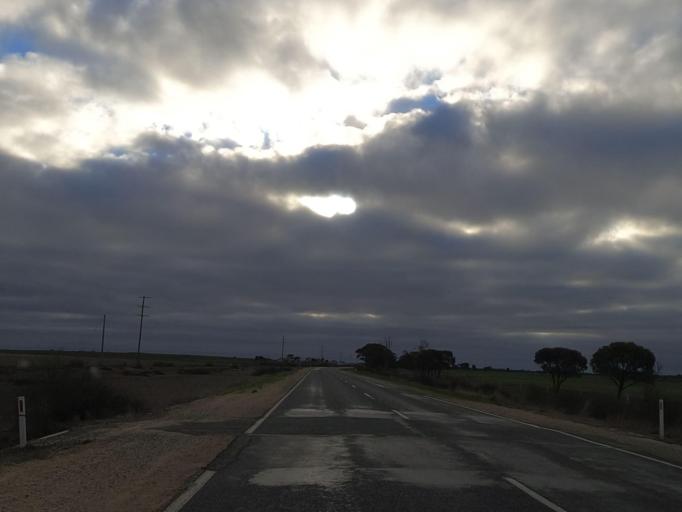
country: AU
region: Victoria
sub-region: Swan Hill
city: Swan Hill
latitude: -35.6481
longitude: 143.8374
